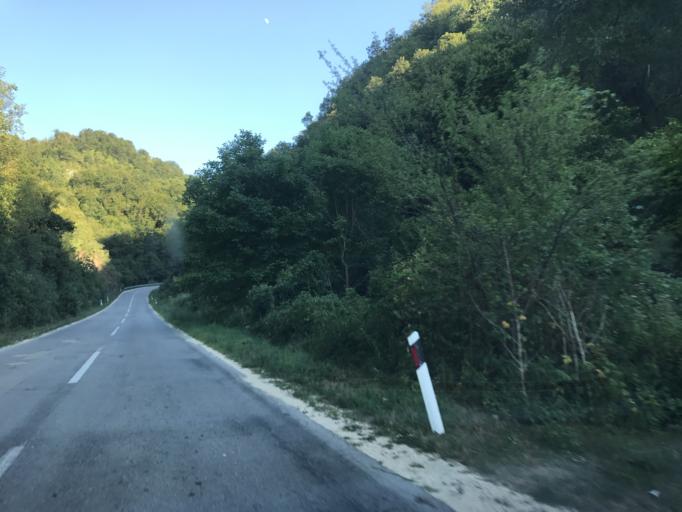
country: RO
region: Mehedinti
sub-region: Comuna Svinita
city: Svinita
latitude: 44.3207
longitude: 22.2111
